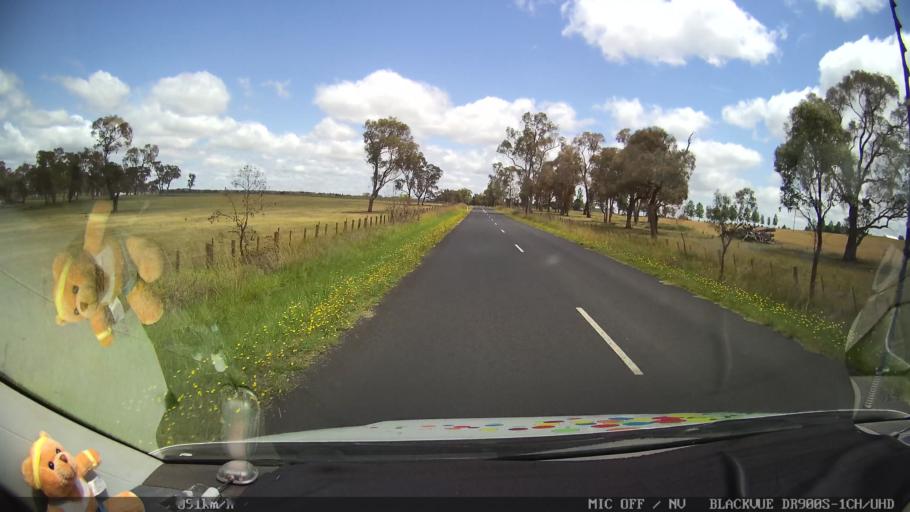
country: AU
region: New South Wales
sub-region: Glen Innes Severn
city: Glen Innes
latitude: -29.6494
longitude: 151.6928
